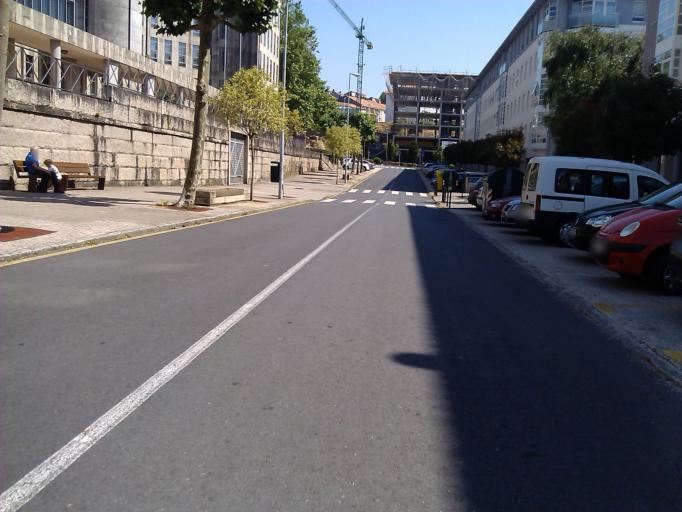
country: ES
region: Galicia
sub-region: Provincia da Coruna
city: Santiago de Compostela
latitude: 42.8828
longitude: -8.5326
